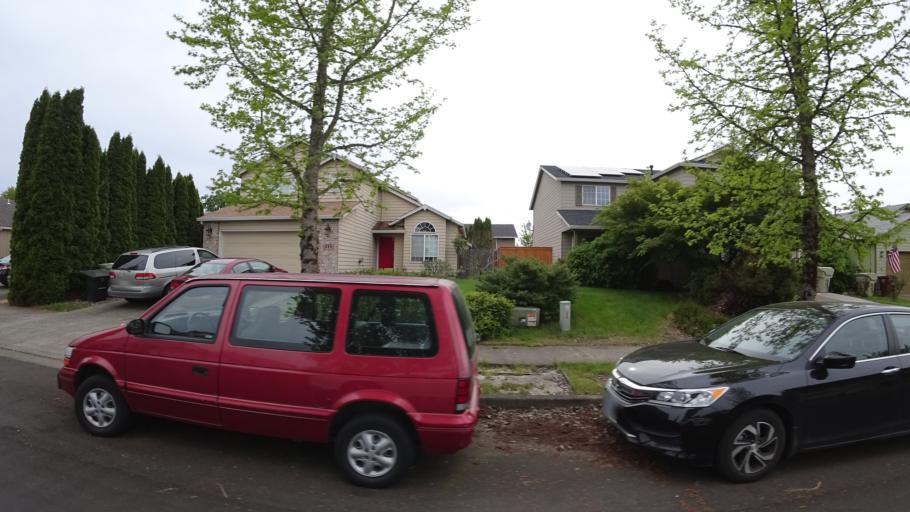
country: US
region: Oregon
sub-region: Washington County
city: Aloha
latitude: 45.5148
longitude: -122.9105
